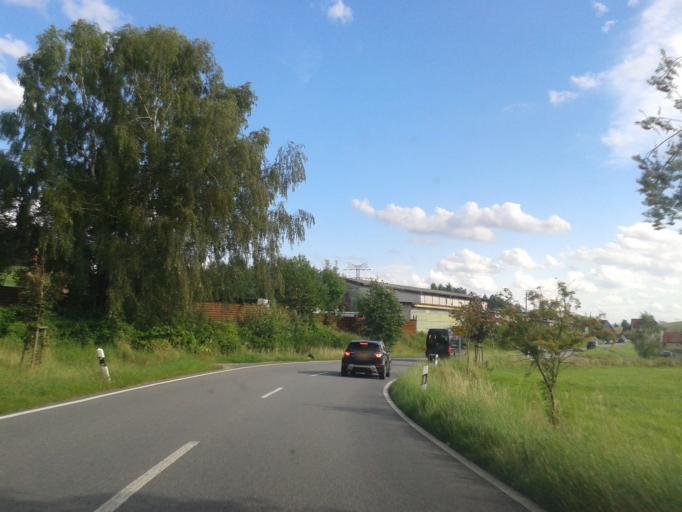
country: DE
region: Saxony
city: Durrrohrsdorf
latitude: 51.0224
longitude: 13.9555
